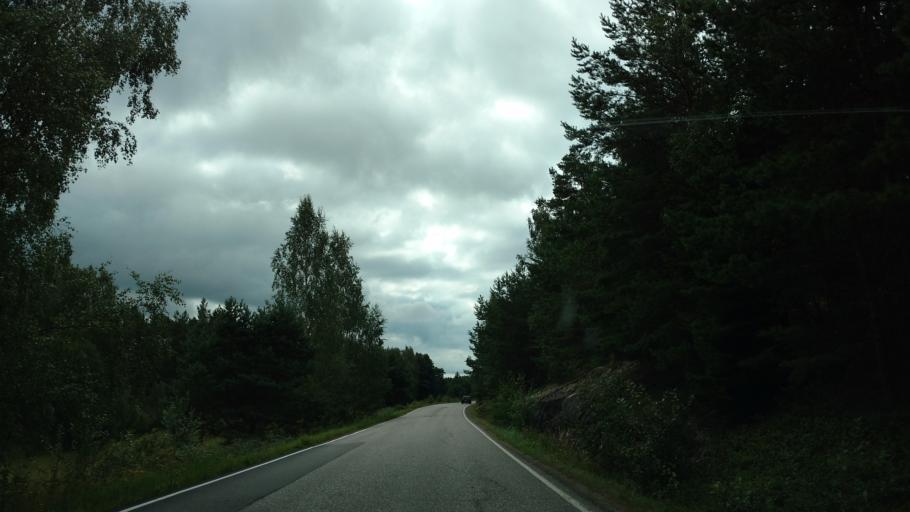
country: FI
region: Varsinais-Suomi
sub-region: Aboland-Turunmaa
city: Dragsfjaerd
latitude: 60.0211
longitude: 22.4591
